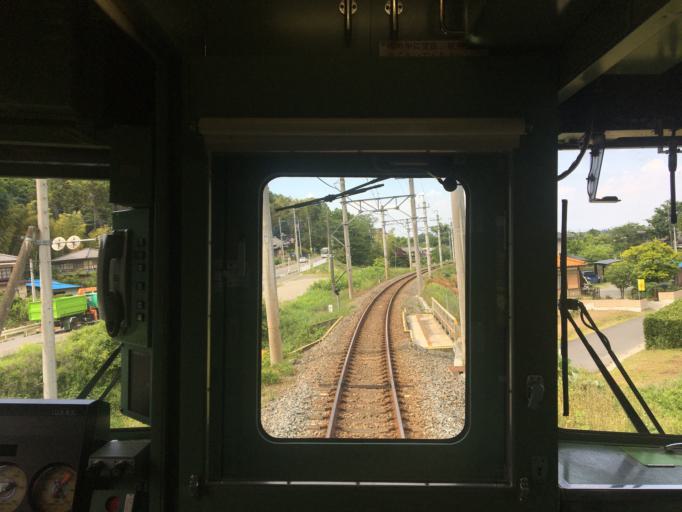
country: JP
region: Saitama
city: Yorii
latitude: 36.0984
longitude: 139.2344
